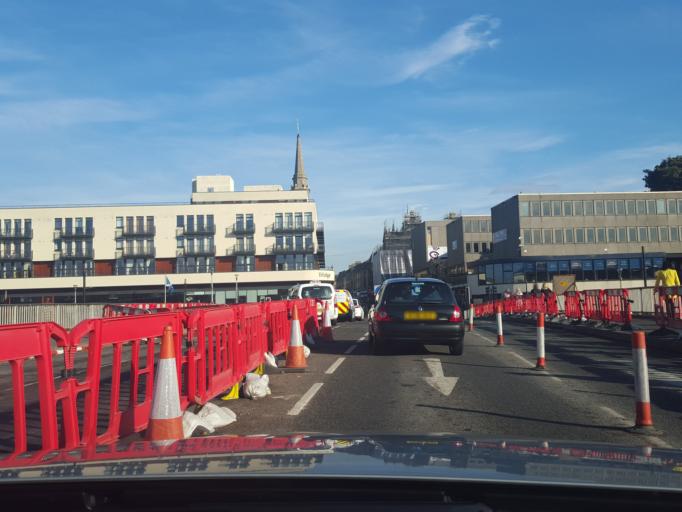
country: GB
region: Scotland
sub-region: Highland
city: Inverness
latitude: 57.4768
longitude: -4.2279
